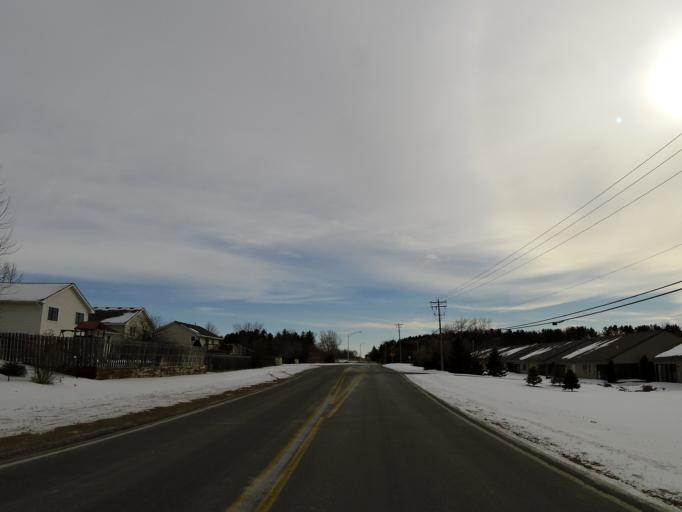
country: US
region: Minnesota
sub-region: Washington County
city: Lakeland
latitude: 44.9509
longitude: -92.7313
